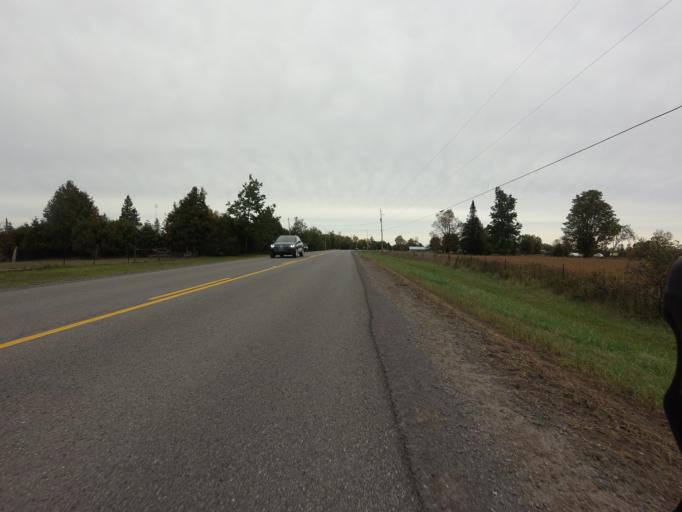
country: CA
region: Ontario
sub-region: Lanark County
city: Smiths Falls
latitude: 44.8385
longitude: -75.8171
